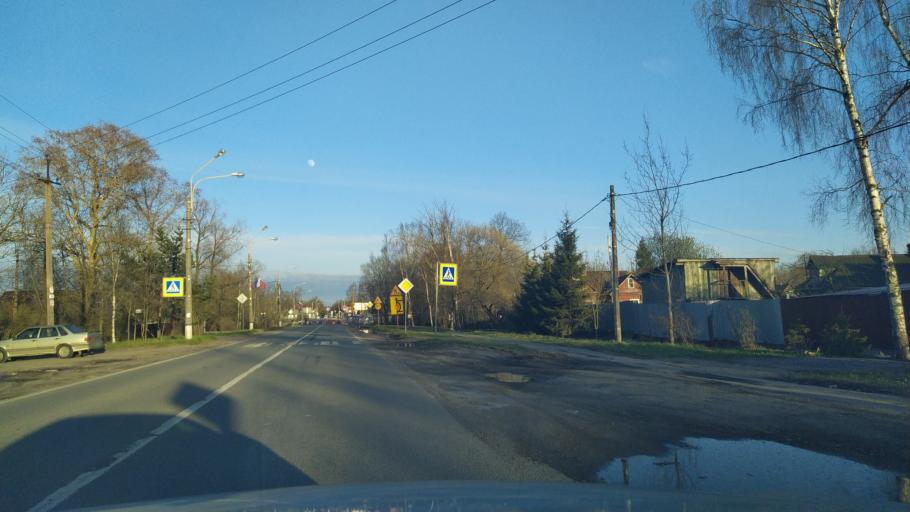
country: RU
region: St.-Petersburg
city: Aleksandrovskaya
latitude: 59.7348
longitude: 30.3368
